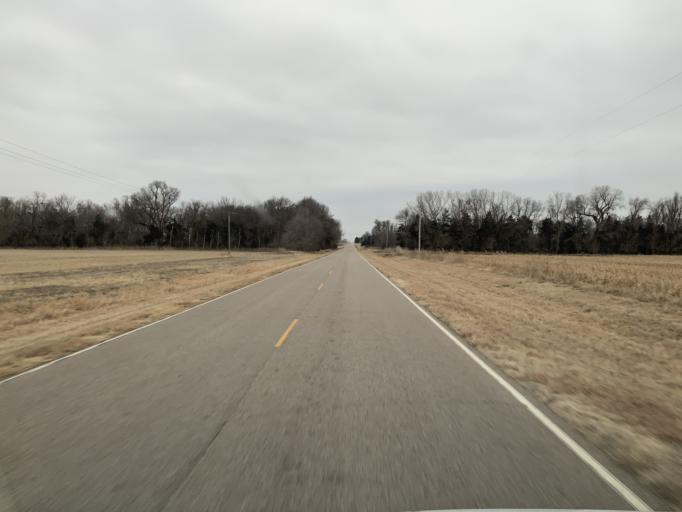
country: US
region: Kansas
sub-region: Reno County
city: South Hutchinson
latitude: 37.9357
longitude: -98.0868
